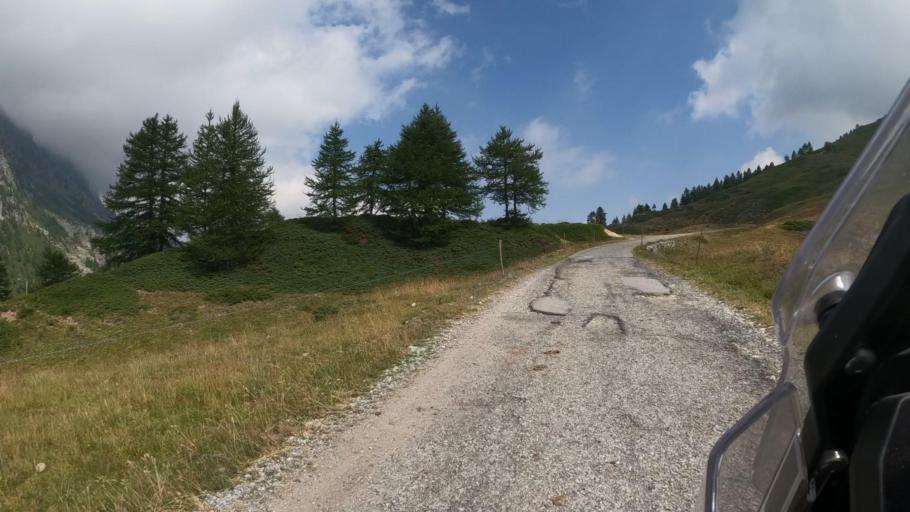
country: IT
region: Piedmont
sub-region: Provincia di Cuneo
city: Marmora
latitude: 44.4013
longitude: 7.1132
